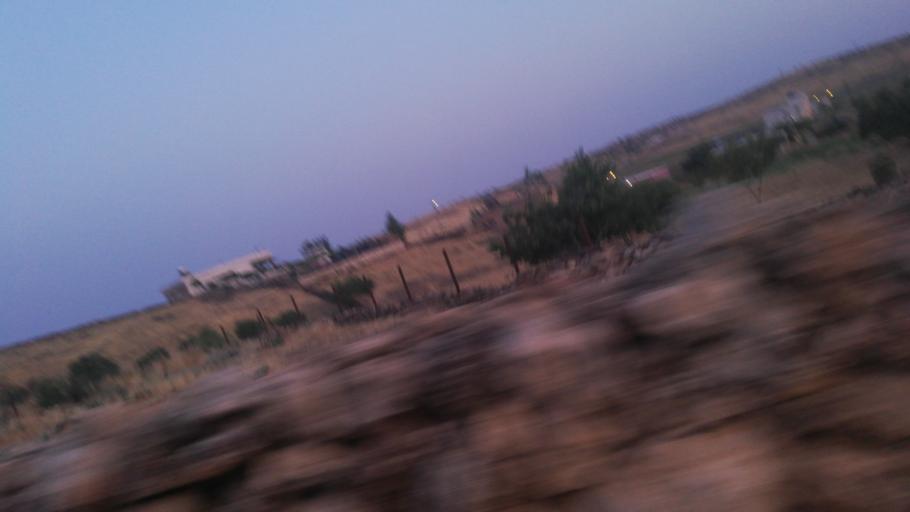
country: TR
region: Mardin
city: Kindirip
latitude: 37.4482
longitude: 41.2241
